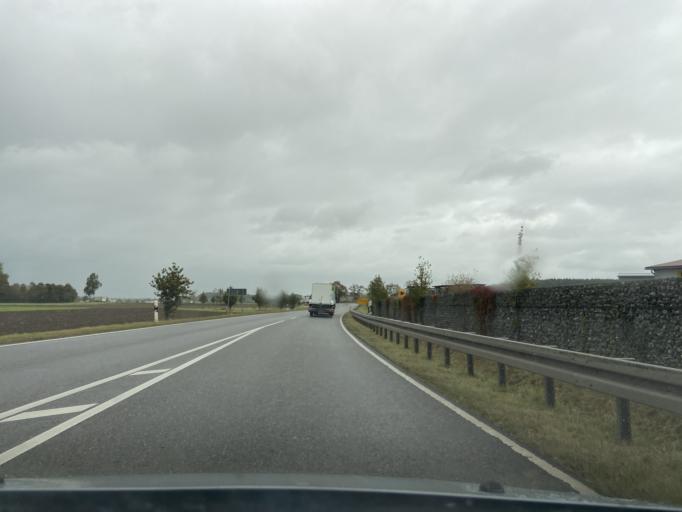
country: DE
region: Baden-Wuerttemberg
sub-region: Tuebingen Region
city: Ennetach
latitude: 48.0319
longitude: 9.2956
